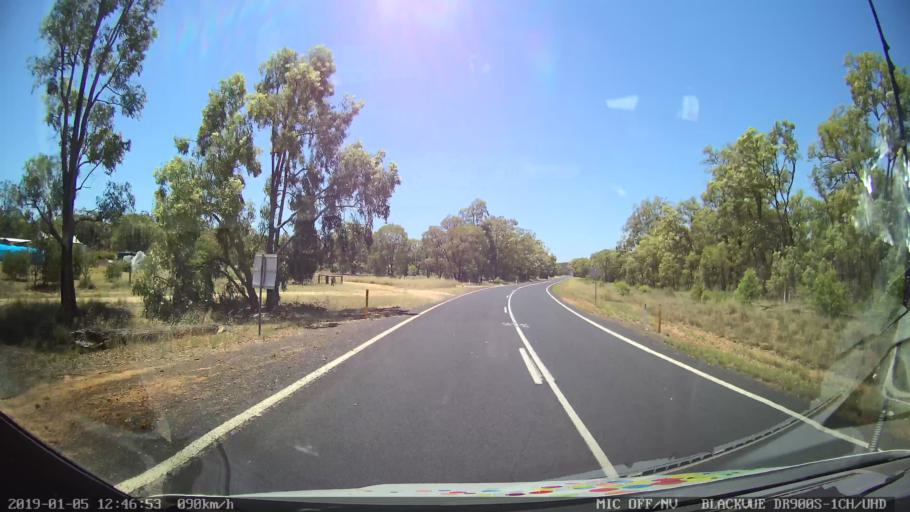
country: AU
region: New South Wales
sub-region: Warrumbungle Shire
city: Coonabarabran
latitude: -31.1146
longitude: 149.5691
